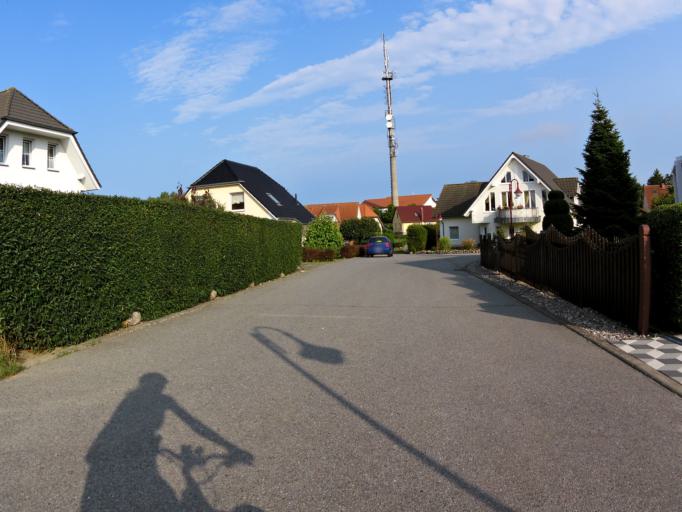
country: DE
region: Mecklenburg-Vorpommern
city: Seebad Bansin
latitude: 53.9567
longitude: 14.1475
